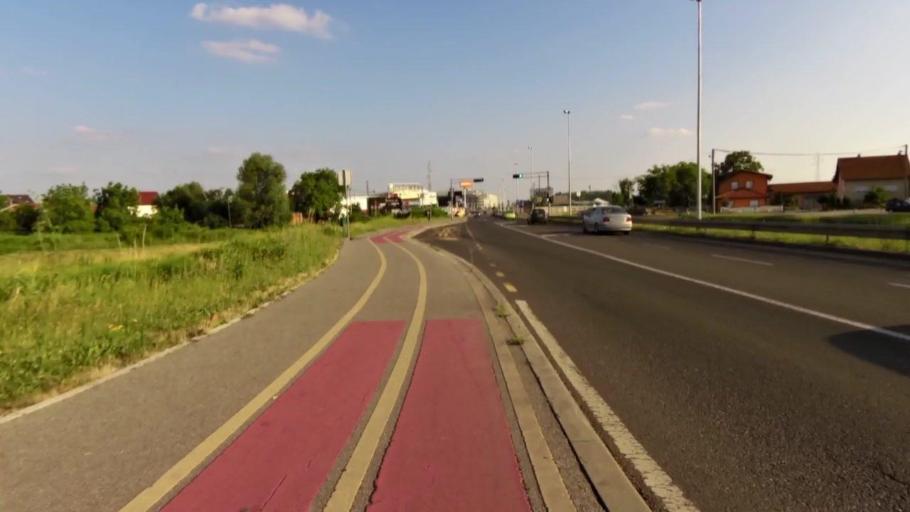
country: HR
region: Grad Zagreb
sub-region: Sesvete
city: Sesvete
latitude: 45.8180
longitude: 16.1019
